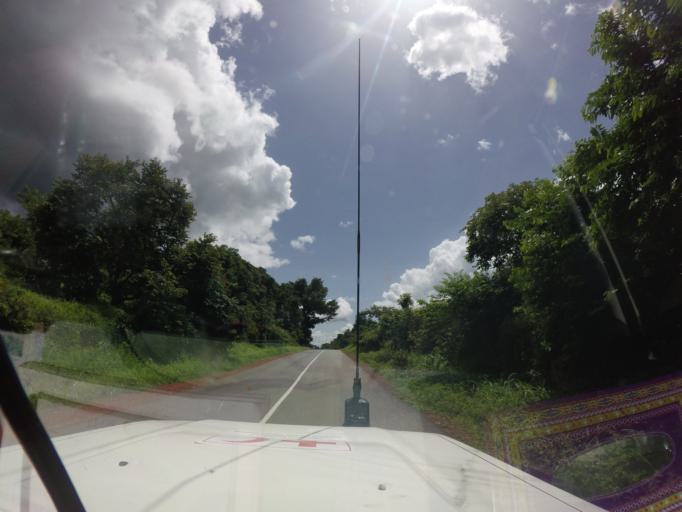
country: SL
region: Northern Province
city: Bindi
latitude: 10.1458
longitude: -11.5876
